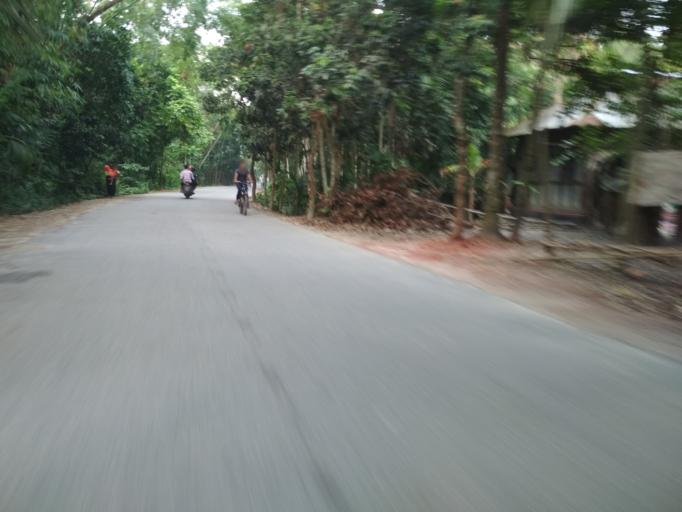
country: BD
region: Chittagong
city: Raipur
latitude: 23.0062
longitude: 90.7091
